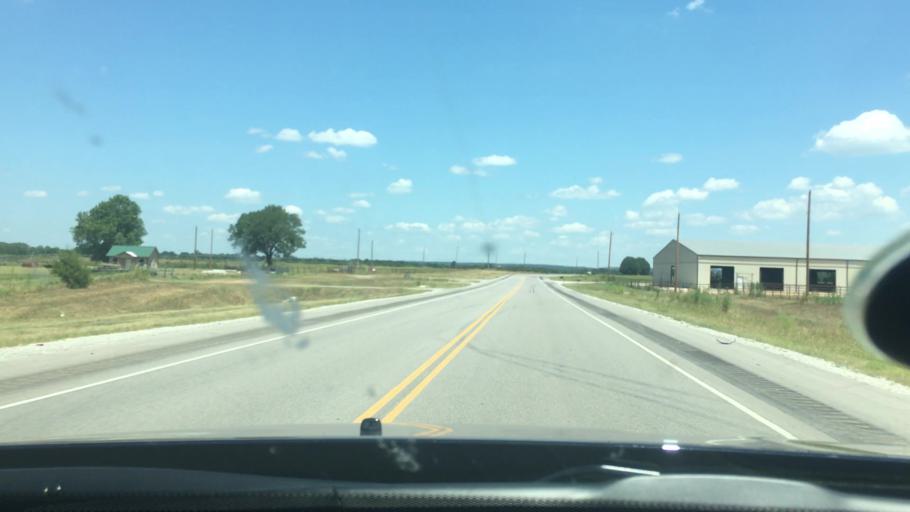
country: US
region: Oklahoma
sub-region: Carter County
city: Dickson
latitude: 34.2362
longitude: -96.9756
